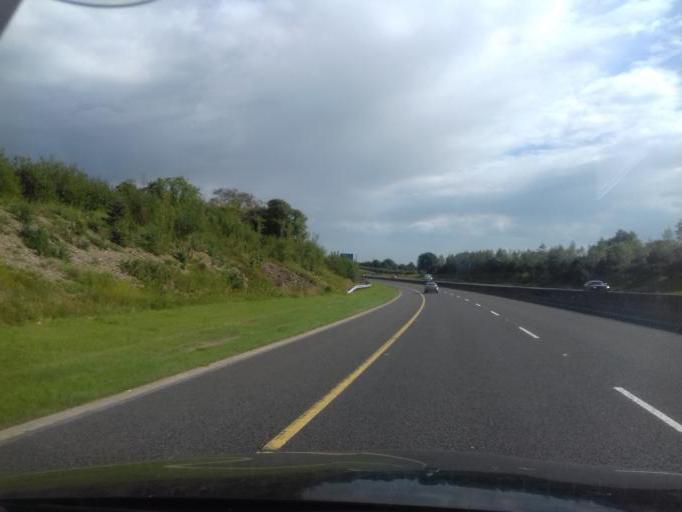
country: IE
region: Leinster
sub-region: Kilkenny
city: Mooncoin
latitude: 52.3847
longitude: -7.1724
